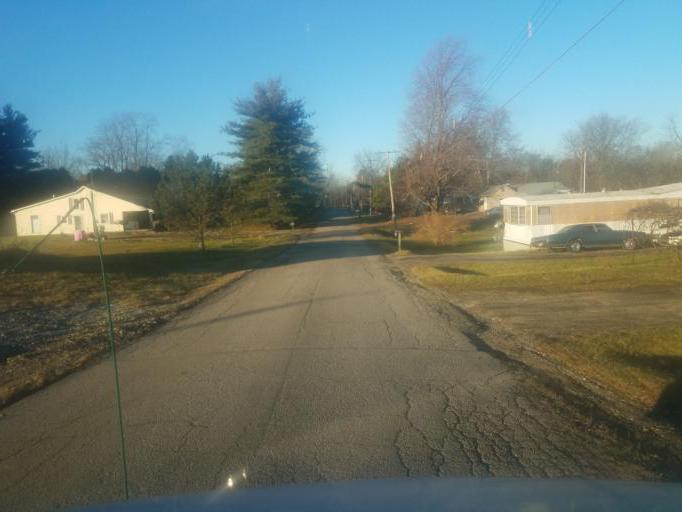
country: US
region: Ohio
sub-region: Richland County
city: Mansfield
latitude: 40.7882
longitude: -82.5461
